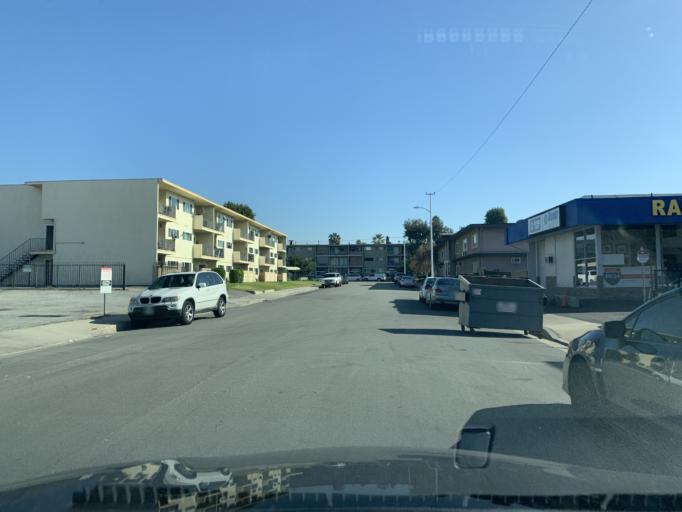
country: US
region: California
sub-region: Los Angeles County
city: Covina
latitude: 34.0896
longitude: -117.8810
